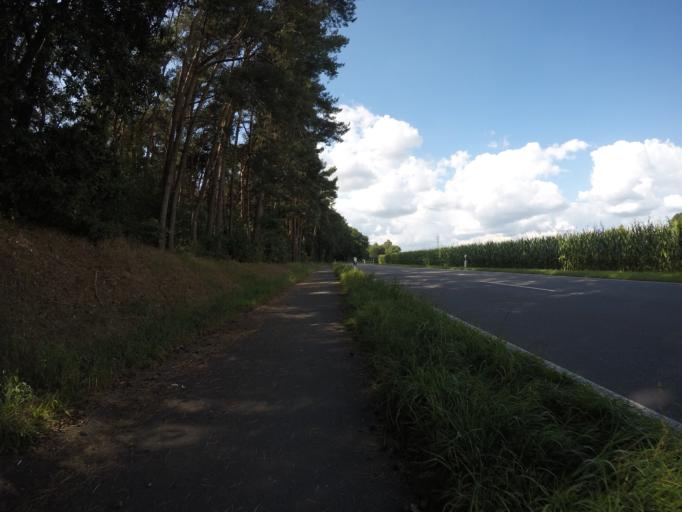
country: DE
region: North Rhine-Westphalia
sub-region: Regierungsbezirk Dusseldorf
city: Mehrhoog
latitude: 51.7487
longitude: 6.5383
